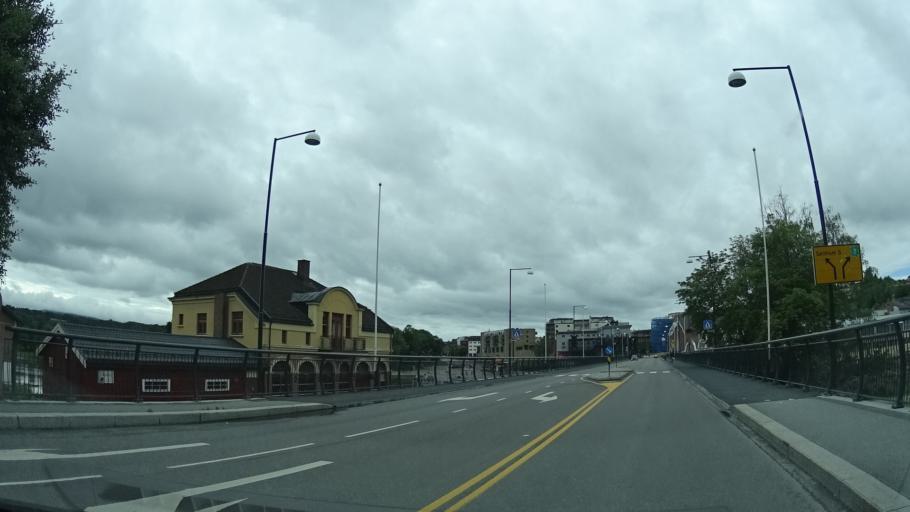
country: NO
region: Buskerud
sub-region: Ringerike
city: Honefoss
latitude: 60.1703
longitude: 10.2583
